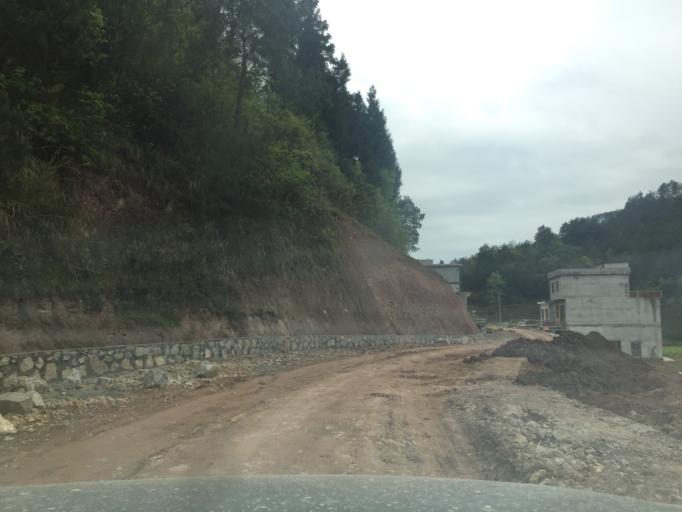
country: CN
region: Guizhou Sheng
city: Fuxing
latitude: 28.0577
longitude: 107.9088
